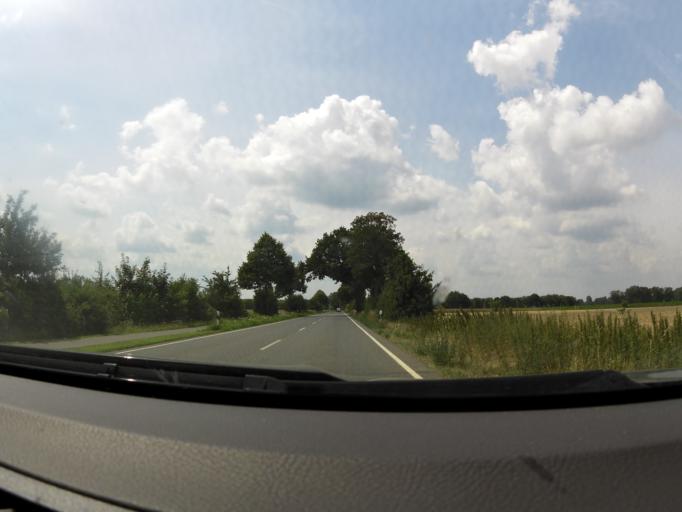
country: DE
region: North Rhine-Westphalia
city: Geldern
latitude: 51.5628
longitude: 6.3443
